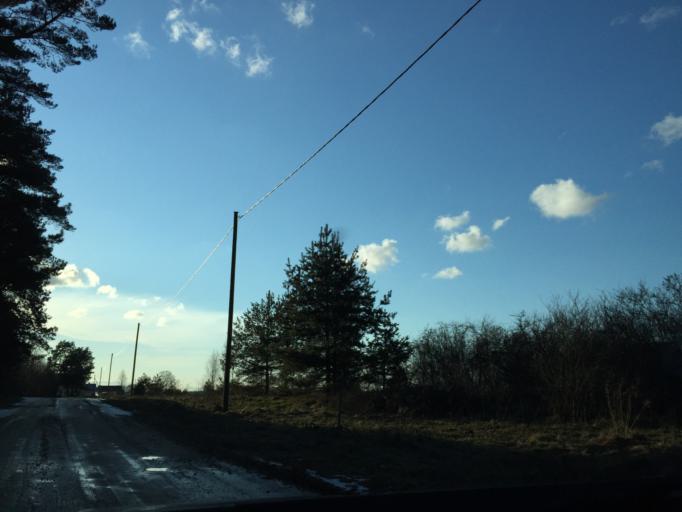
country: LV
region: Kekava
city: Kekava
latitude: 56.8742
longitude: 24.2091
